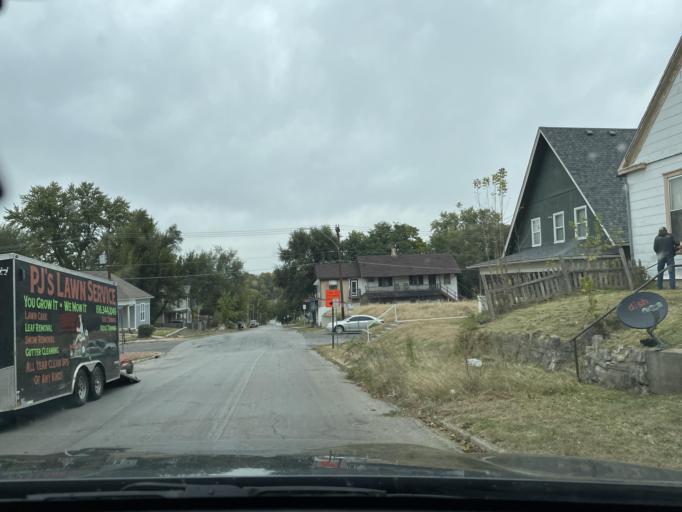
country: US
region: Missouri
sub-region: Buchanan County
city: Saint Joseph
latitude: 39.7765
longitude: -94.8442
